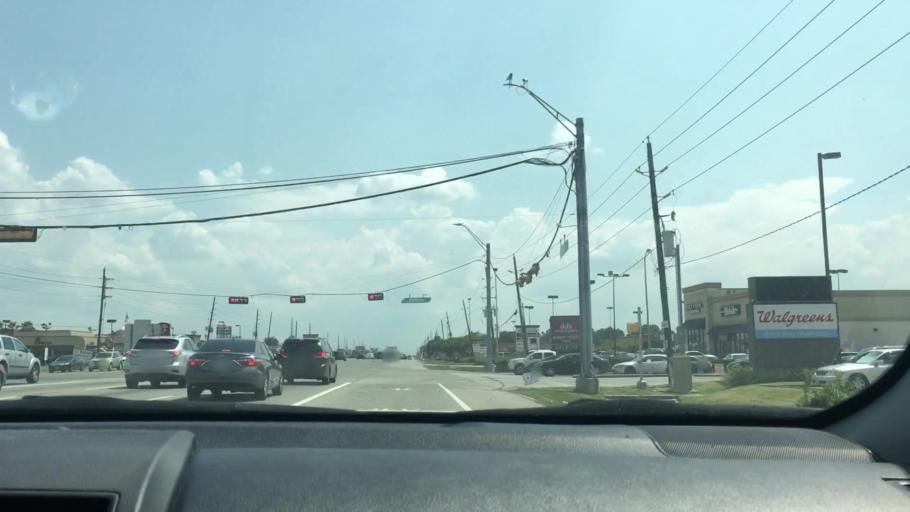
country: US
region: Texas
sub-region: Fort Bend County
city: Mission Bend
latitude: 29.7045
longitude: -95.6442
